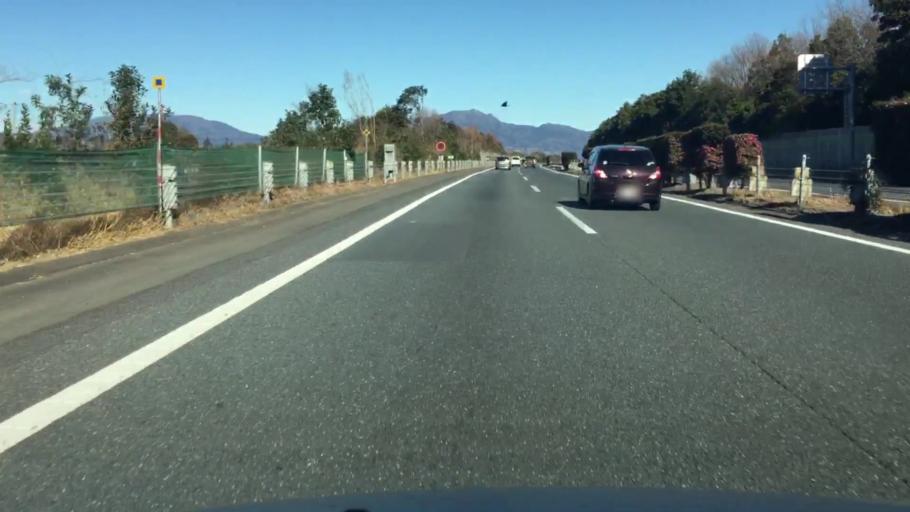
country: JP
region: Gunma
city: Kanekomachi
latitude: 36.4352
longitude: 139.0143
